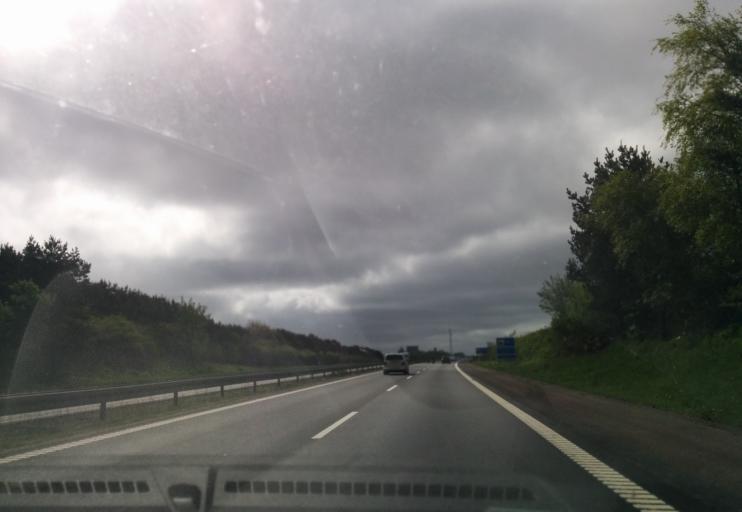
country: DK
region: South Denmark
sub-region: Fredericia Kommune
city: Taulov
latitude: 55.5539
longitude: 9.6349
